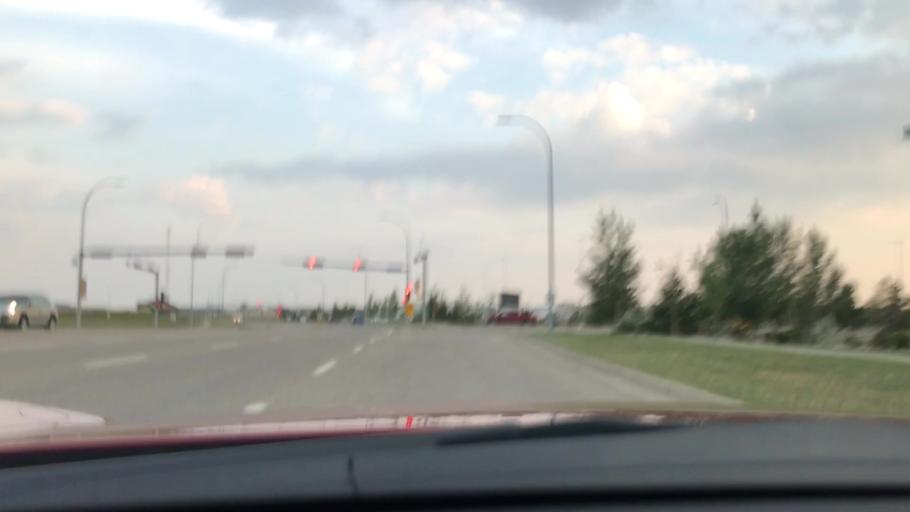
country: CA
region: Alberta
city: Airdrie
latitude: 51.2085
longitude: -113.9905
